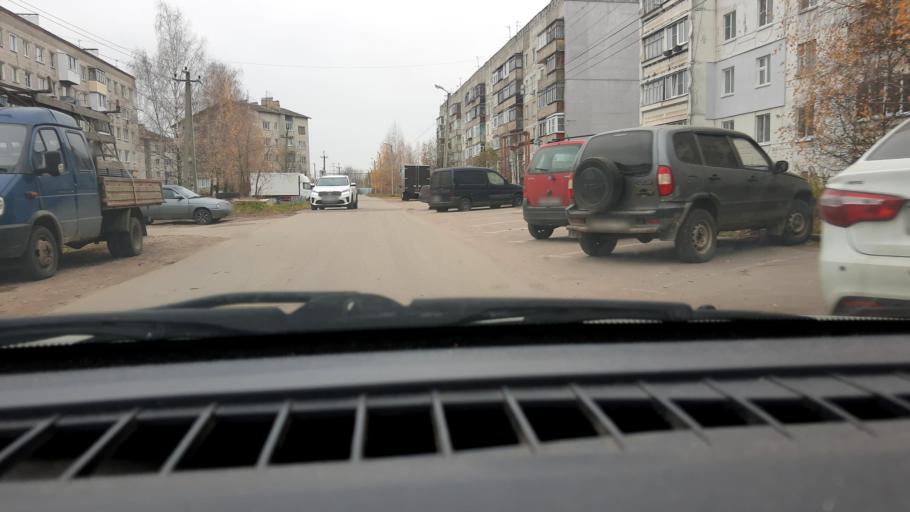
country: RU
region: Nizjnij Novgorod
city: Afonino
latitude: 56.2090
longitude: 44.0979
